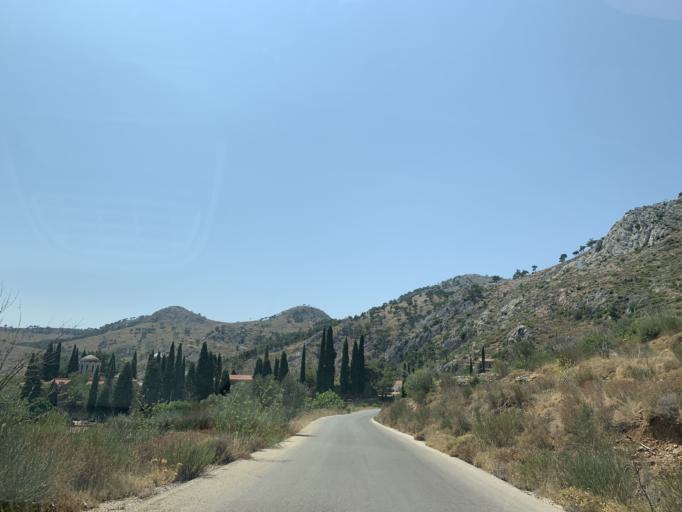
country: GR
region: North Aegean
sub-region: Chios
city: Chios
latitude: 38.3762
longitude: 26.0558
